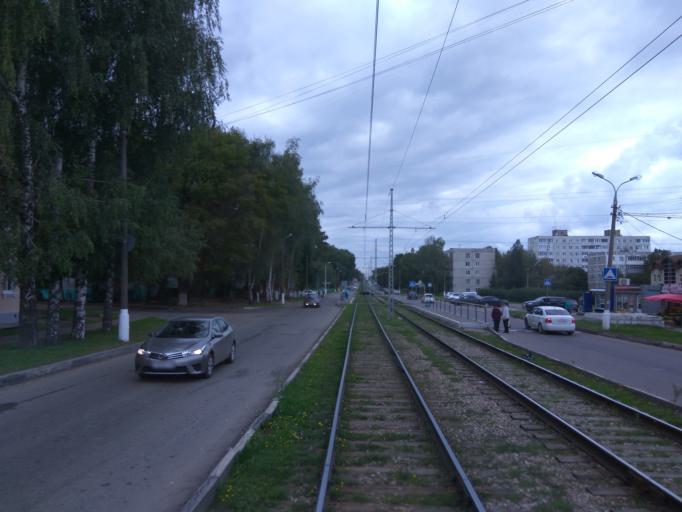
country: RU
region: Moskovskaya
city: Kolomna
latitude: 55.0785
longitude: 38.7703
